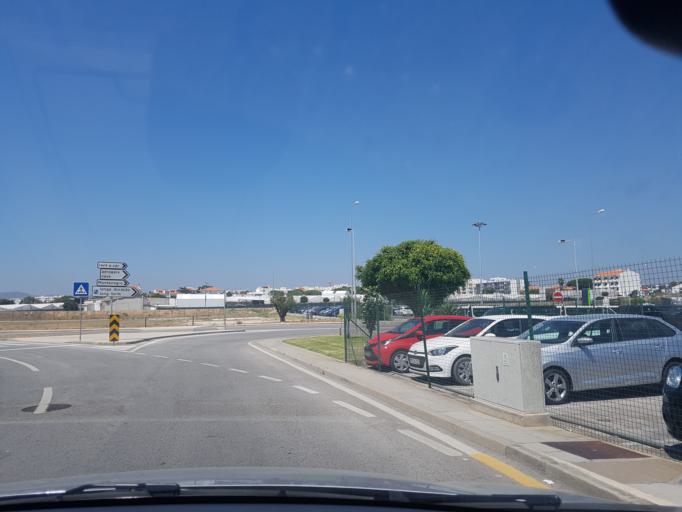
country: PT
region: Faro
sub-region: Faro
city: Faro
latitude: 37.0215
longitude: -7.9659
